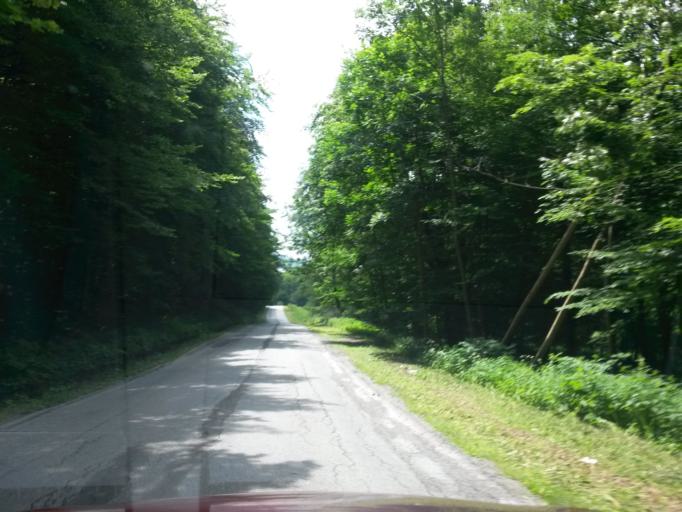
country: SK
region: Kosicky
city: Gelnica
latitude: 48.9158
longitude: 21.0320
